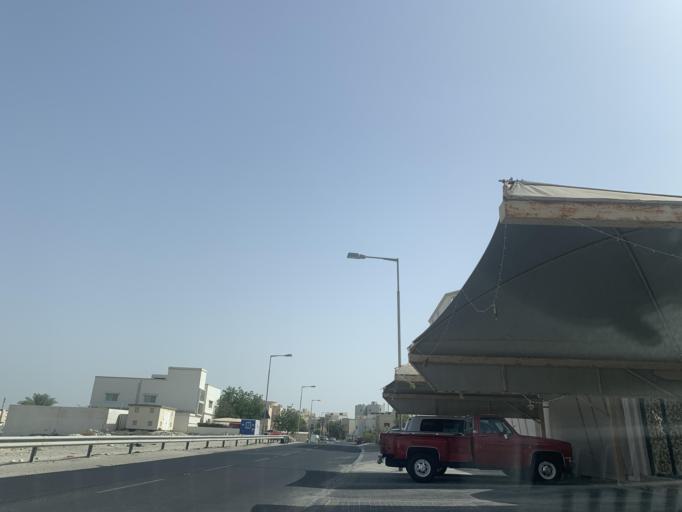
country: BH
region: Northern
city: Ar Rifa'
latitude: 26.1471
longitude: 50.5694
